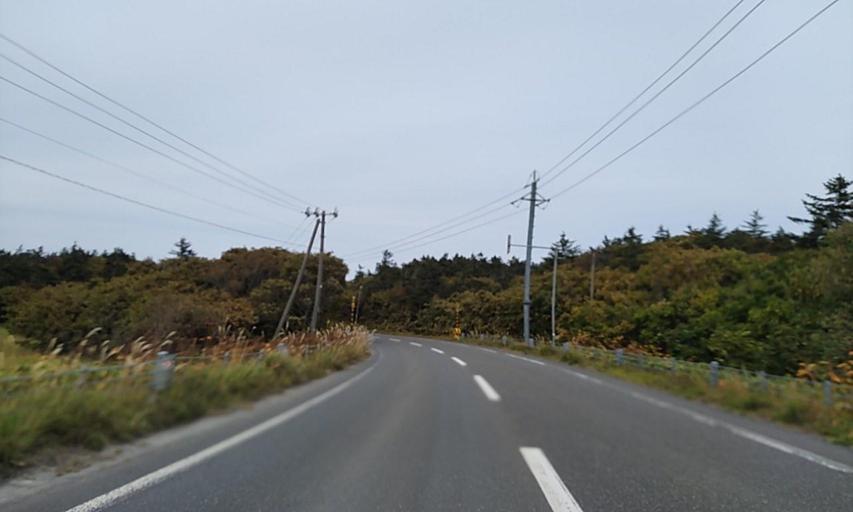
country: JP
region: Hokkaido
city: Makubetsu
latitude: 44.9978
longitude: 141.6957
